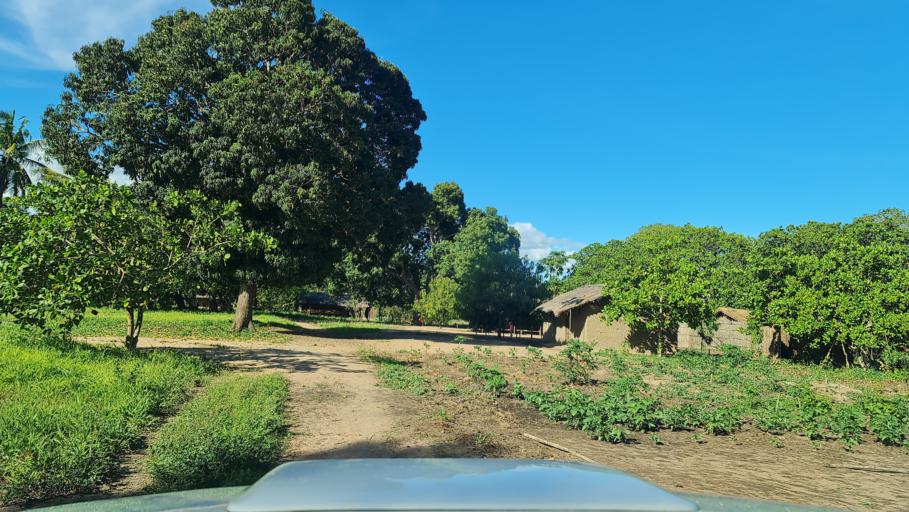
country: MZ
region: Nampula
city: Ilha de Mocambique
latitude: -15.2459
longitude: 40.1795
